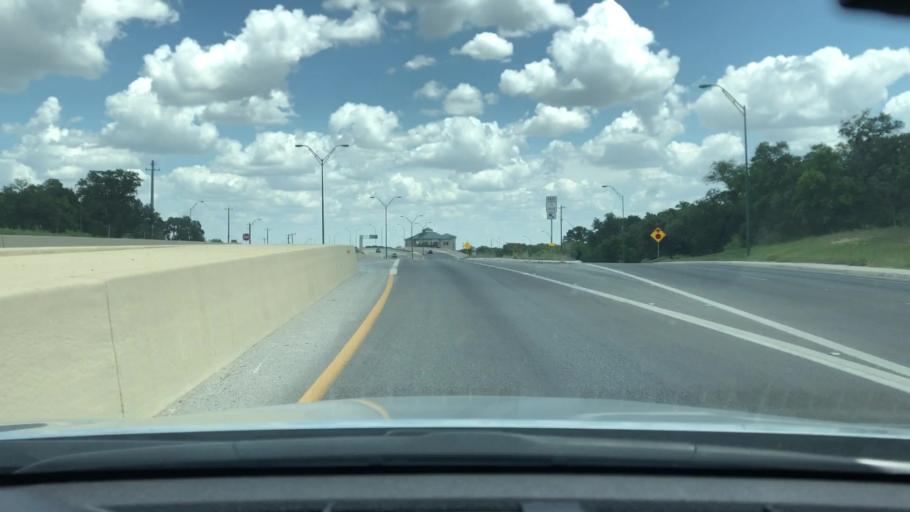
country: US
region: Texas
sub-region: Bexar County
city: Castle Hills
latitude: 29.5569
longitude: -98.4900
